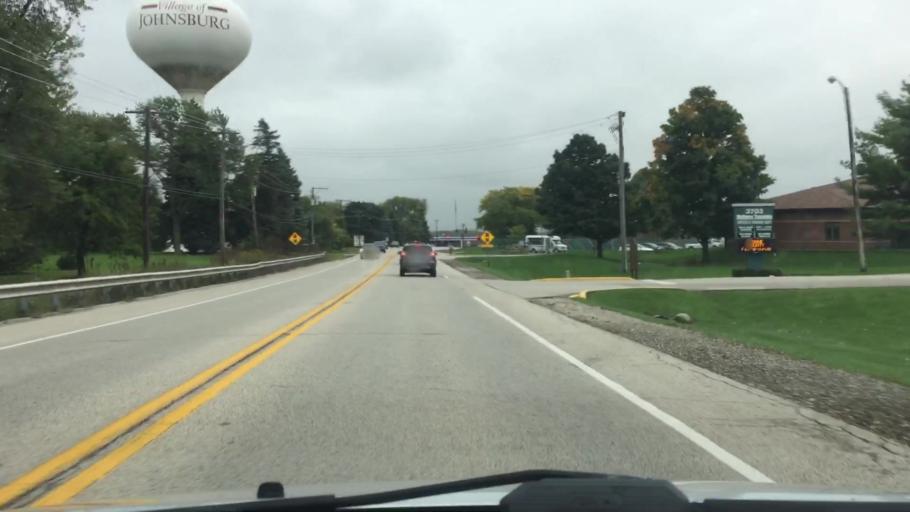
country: US
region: Illinois
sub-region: McHenry County
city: McCullom Lake
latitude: 42.3811
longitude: -88.2724
